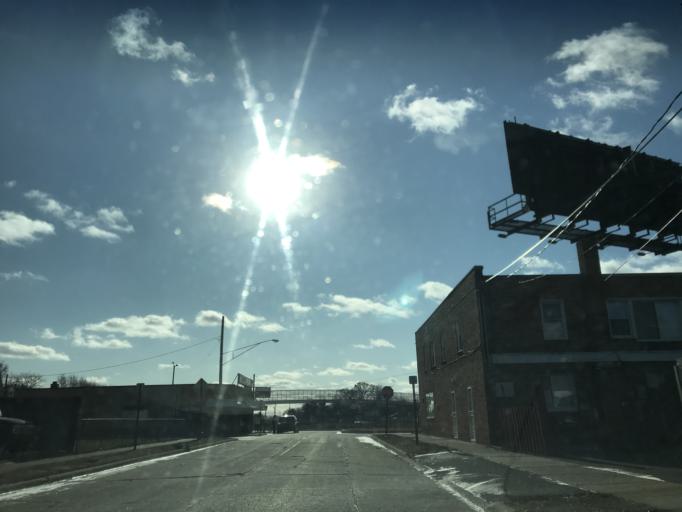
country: US
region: Michigan
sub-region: Oakland County
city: Hazel Park
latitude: 42.4575
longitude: -83.0964
